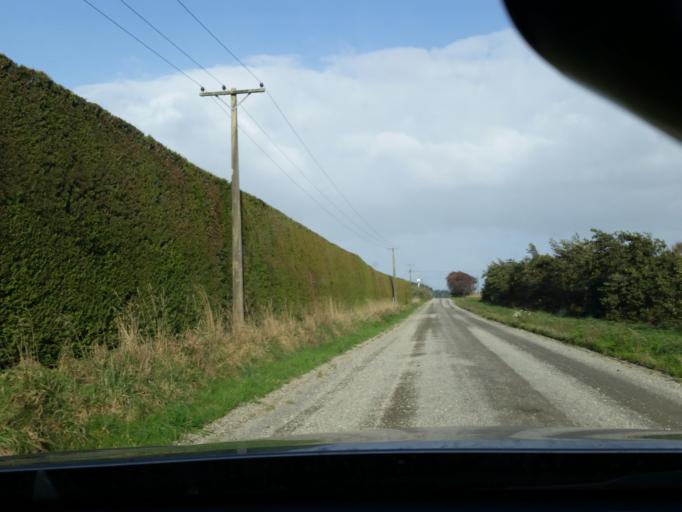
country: NZ
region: Southland
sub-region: Invercargill City
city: Invercargill
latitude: -46.3005
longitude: 168.3034
